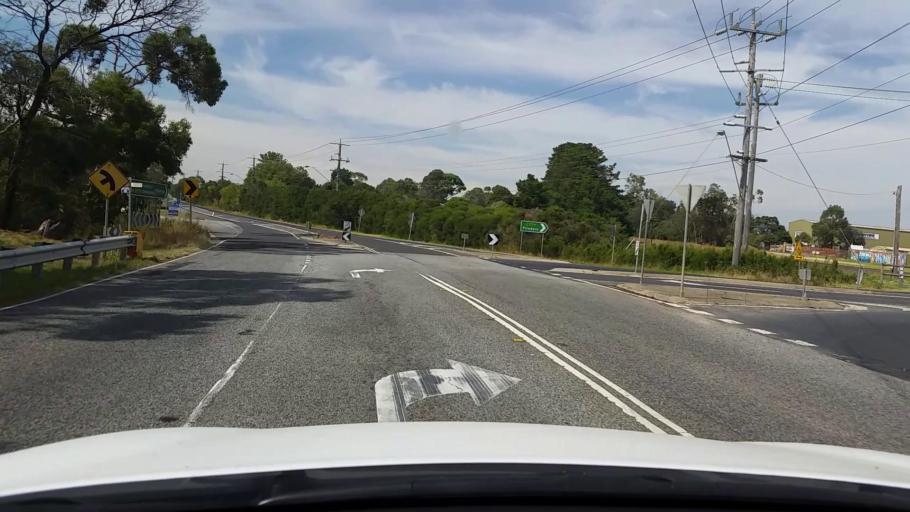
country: AU
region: Victoria
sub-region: Mornington Peninsula
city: Hastings
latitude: -38.2851
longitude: 145.1885
